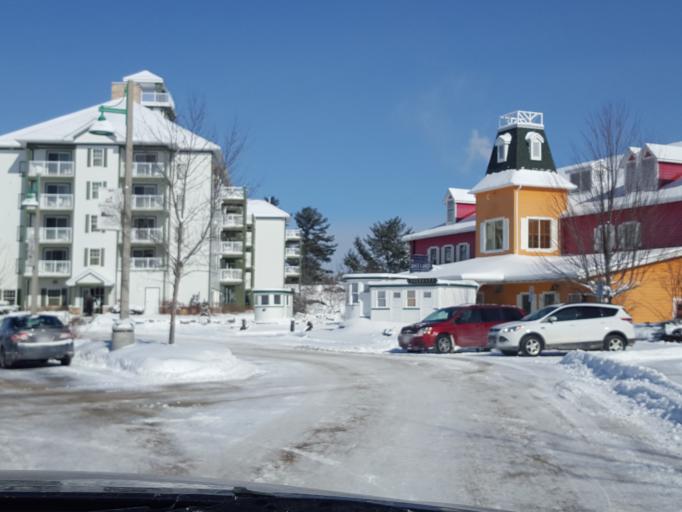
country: CA
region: Ontario
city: Gravenhurst
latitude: 44.9195
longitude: -79.3899
